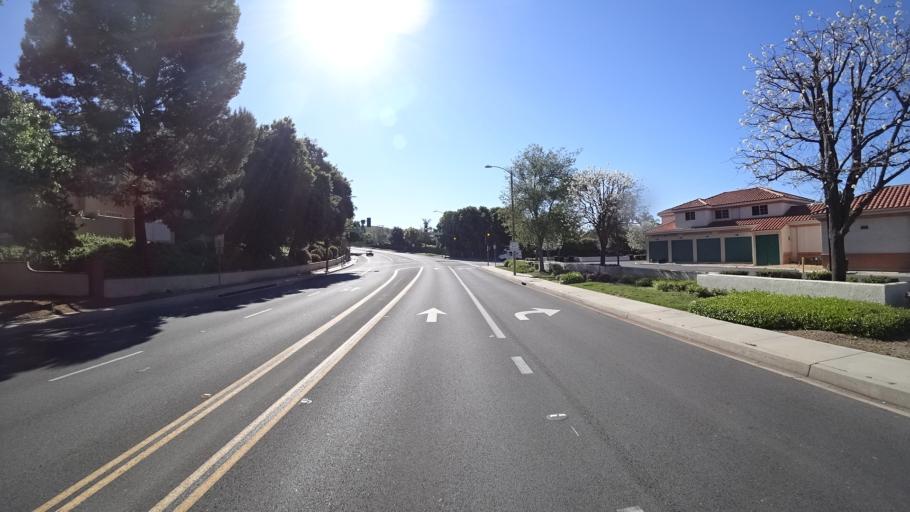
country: US
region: California
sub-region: Ventura County
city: Thousand Oaks
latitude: 34.1721
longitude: -118.8328
